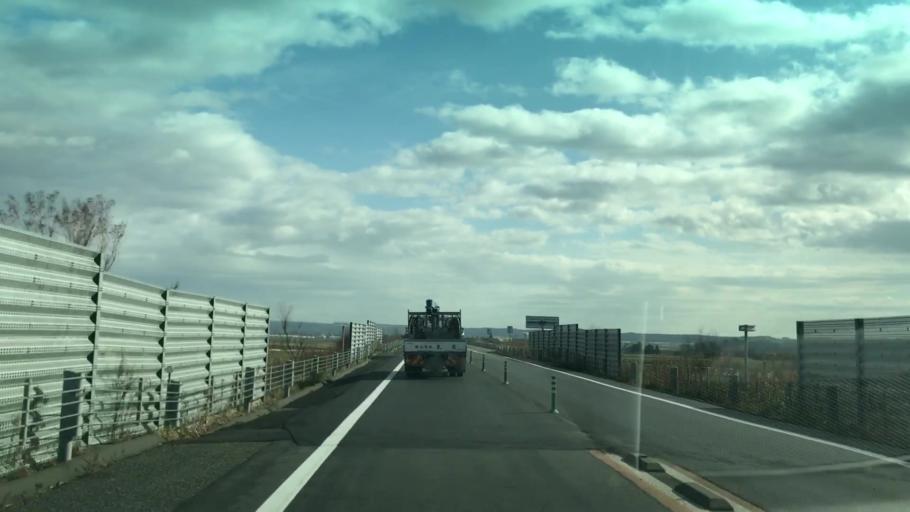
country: JP
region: Hokkaido
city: Tomakomai
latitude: 42.5788
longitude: 141.9569
